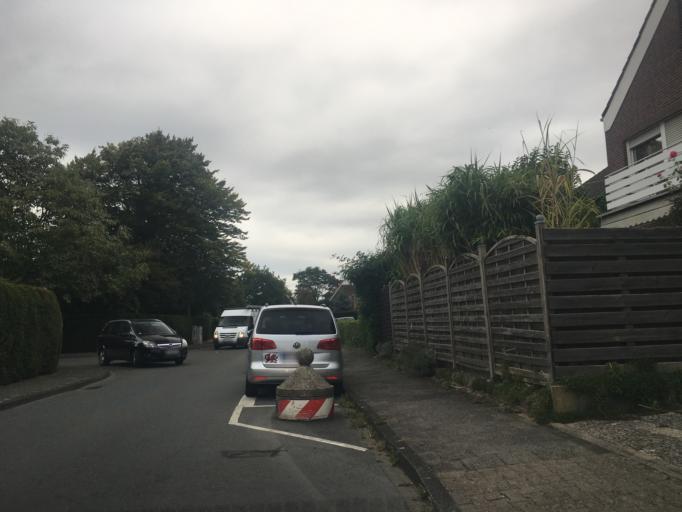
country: DE
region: North Rhine-Westphalia
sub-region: Regierungsbezirk Munster
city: Muenster
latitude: 51.9534
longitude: 7.5422
